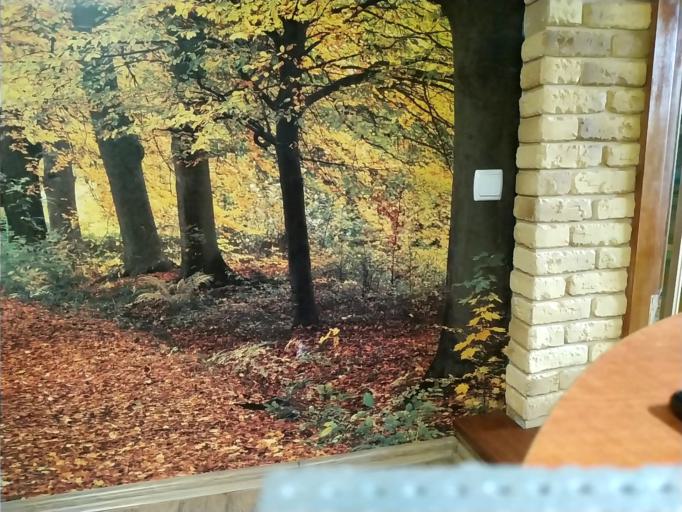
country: RU
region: Vladimir
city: Bavleny
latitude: 56.3674
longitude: 39.5626
